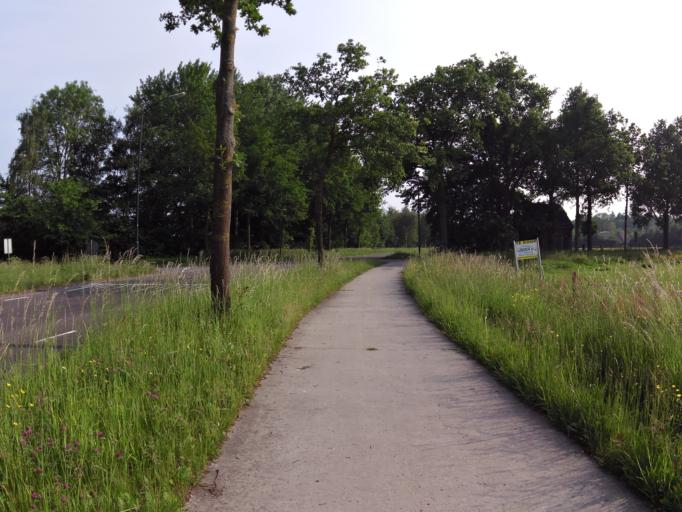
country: NL
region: North Brabant
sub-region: Gemeente Haaren
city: Haaren
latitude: 51.6532
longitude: 5.2191
